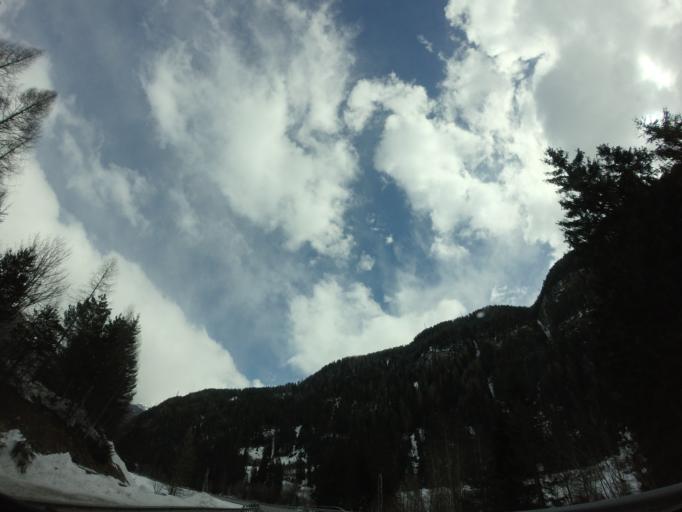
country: AT
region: Tyrol
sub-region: Politischer Bezirk Landeck
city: Nauders
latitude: 46.8736
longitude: 10.4530
